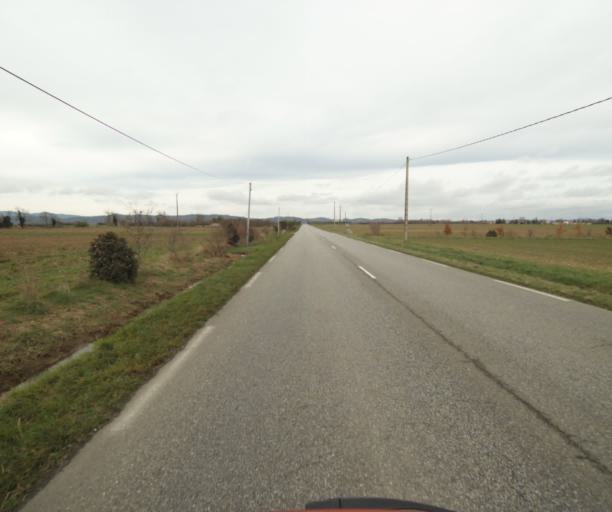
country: FR
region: Midi-Pyrenees
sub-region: Departement de l'Ariege
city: La Tour-du-Crieu
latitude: 43.0943
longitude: 1.6705
